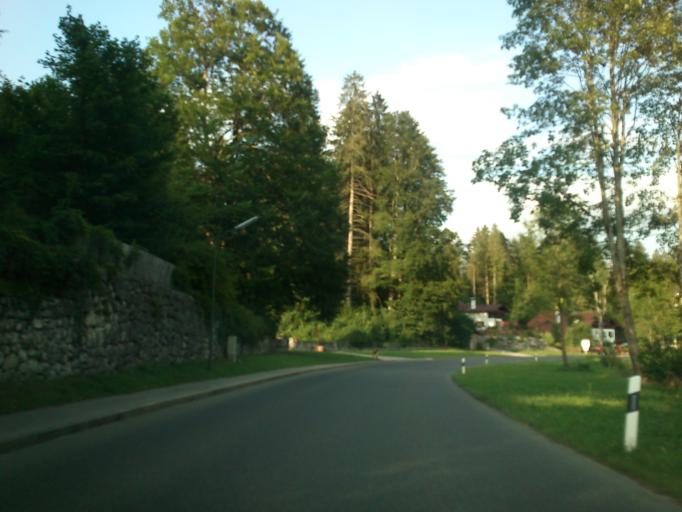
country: DE
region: Bavaria
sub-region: Upper Bavaria
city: Grainau
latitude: 47.4804
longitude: 11.0314
